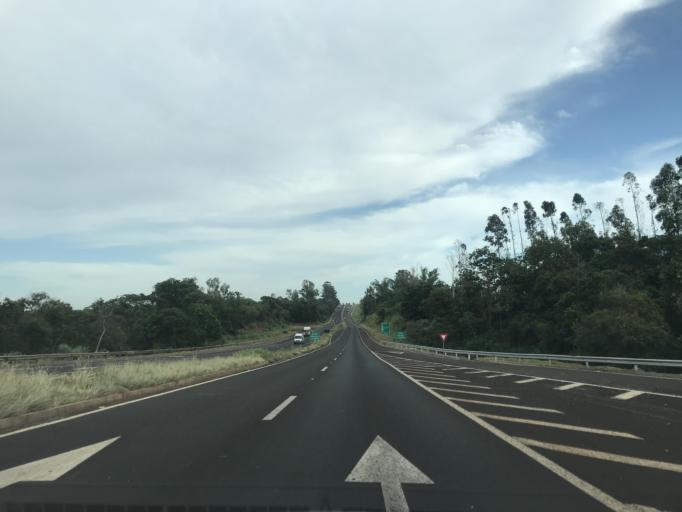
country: BR
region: Parana
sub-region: Alto Parana
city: Alto Parana
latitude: -23.1405
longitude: -52.2862
